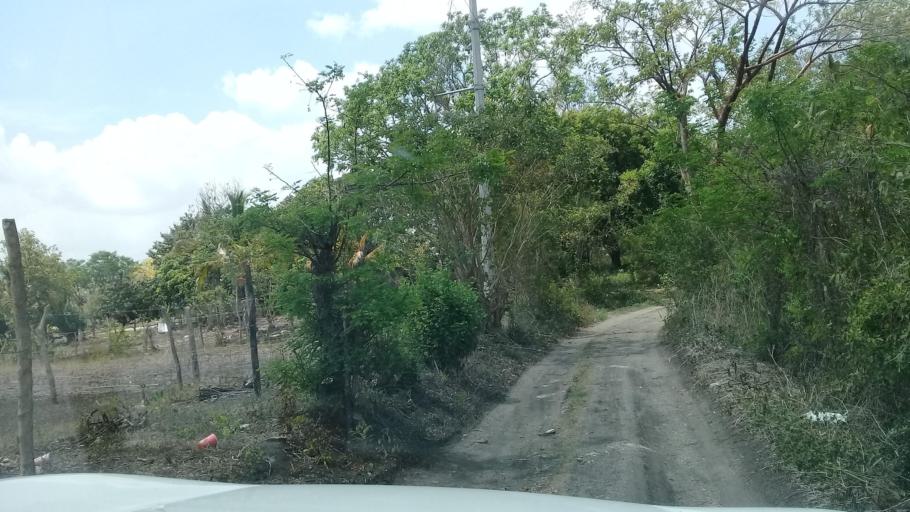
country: MX
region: Veracruz
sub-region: Emiliano Zapata
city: Plan del Rio
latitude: 19.3536
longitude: -96.6437
